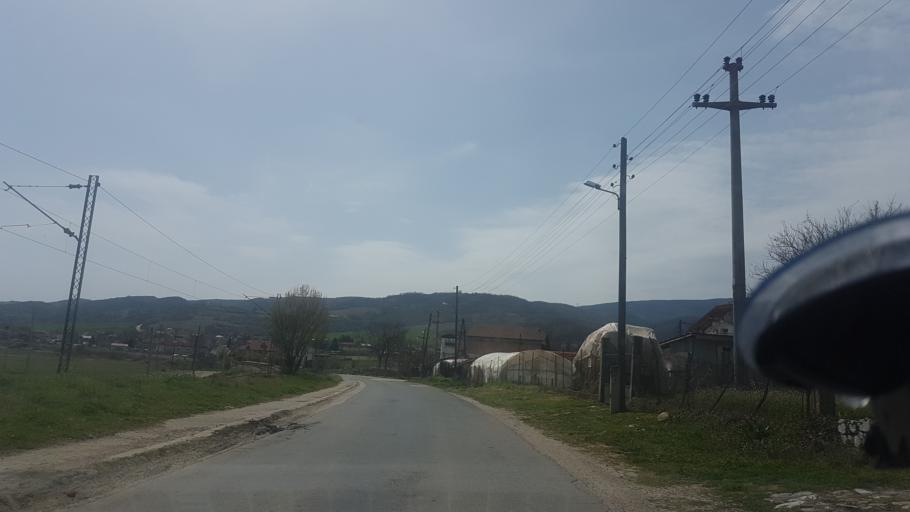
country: MK
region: Zelenikovo
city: Zelenikovo
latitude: 41.8873
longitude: 21.5878
